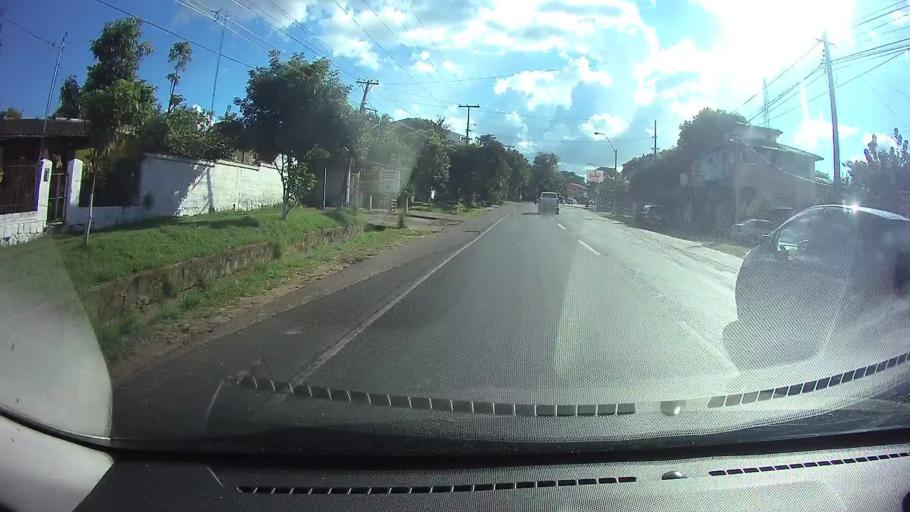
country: PY
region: Cordillera
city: Caacupe
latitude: -25.3879
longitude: -57.1467
